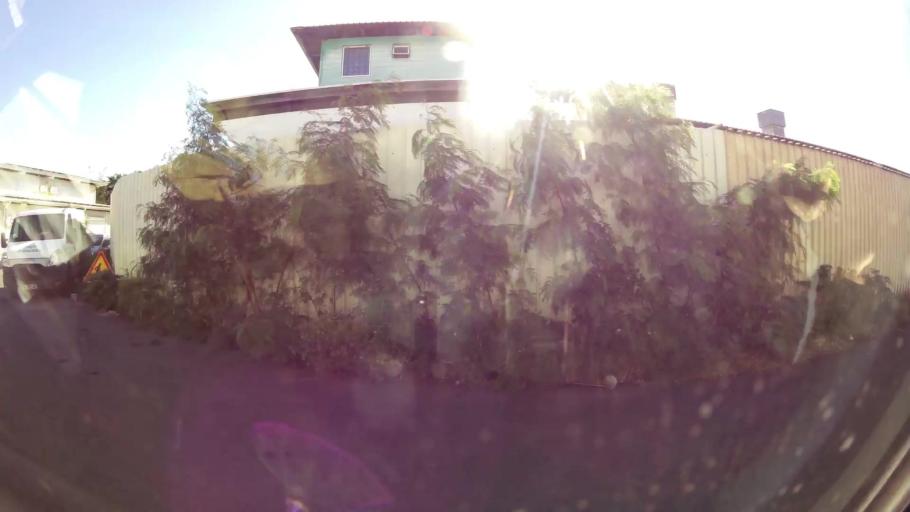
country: YT
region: Mamoudzou
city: Mamoudzou
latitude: -12.7684
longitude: 45.2291
